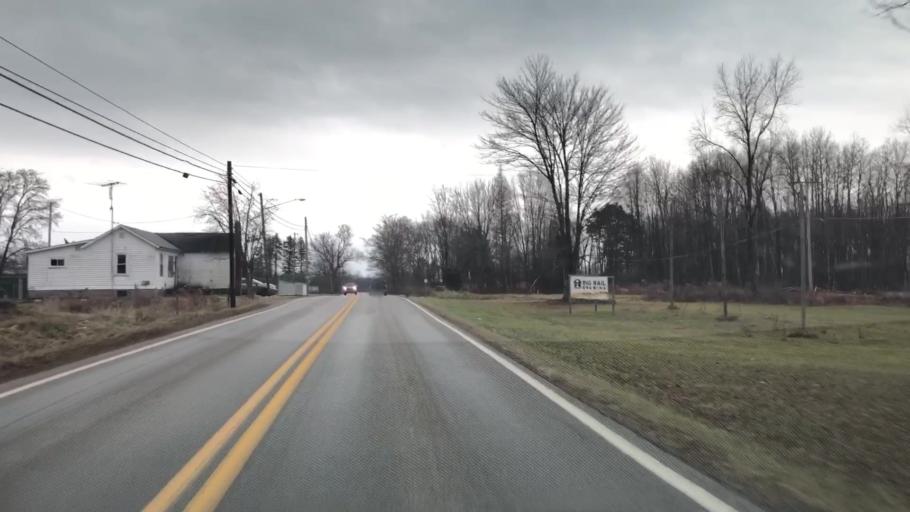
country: US
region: Pennsylvania
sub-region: Mercer County
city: Grove City
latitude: 41.1345
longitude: -80.1343
